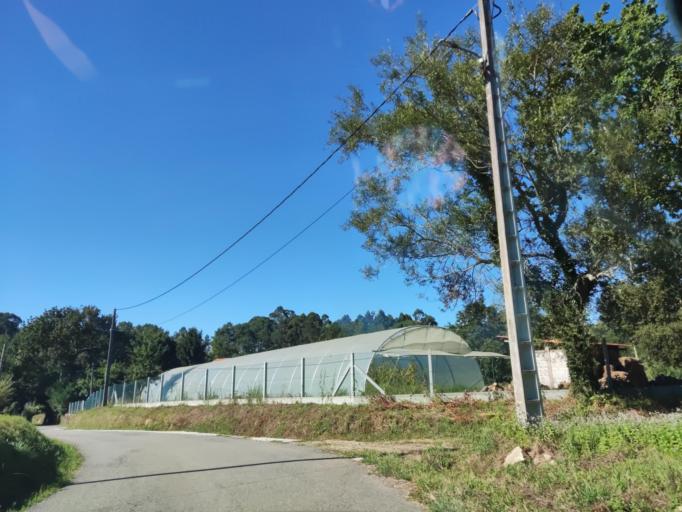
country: ES
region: Galicia
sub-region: Provincia da Coruna
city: Rianxo
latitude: 42.6907
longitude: -8.8470
